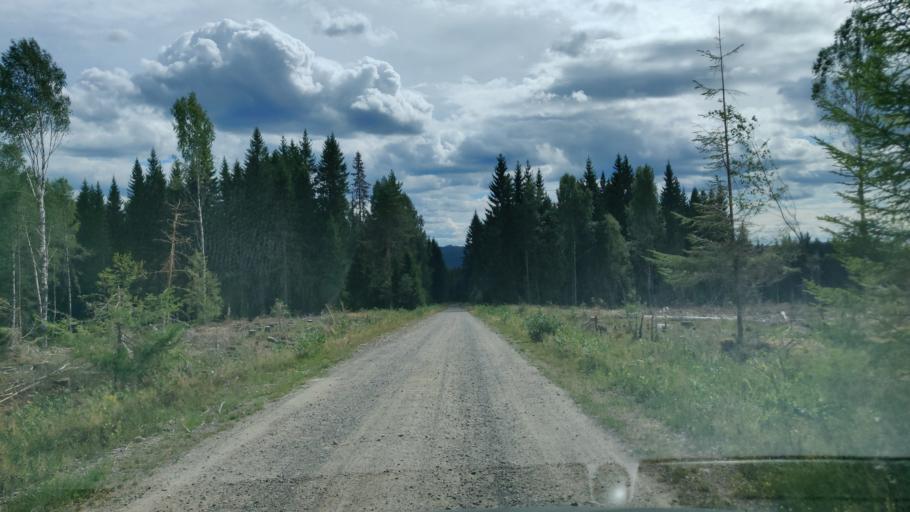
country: SE
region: Vaermland
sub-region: Hagfors Kommun
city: Hagfors
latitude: 60.0075
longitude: 13.7272
